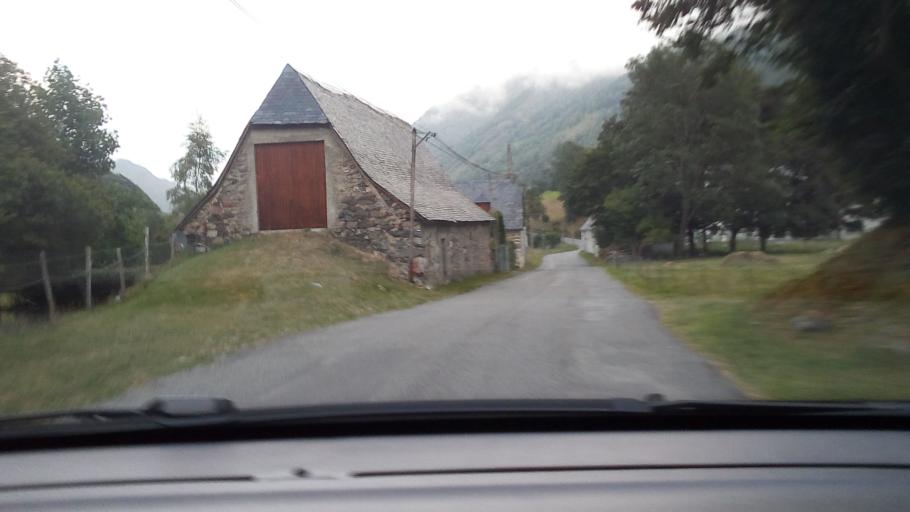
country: FR
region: Midi-Pyrenees
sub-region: Departement des Hautes-Pyrenees
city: Cauterets
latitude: 42.9175
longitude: -0.1886
